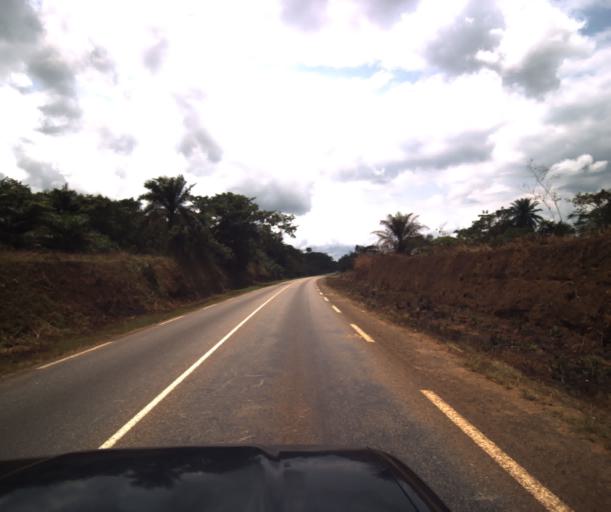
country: CM
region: Centre
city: Eseka
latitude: 3.8488
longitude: 10.4966
